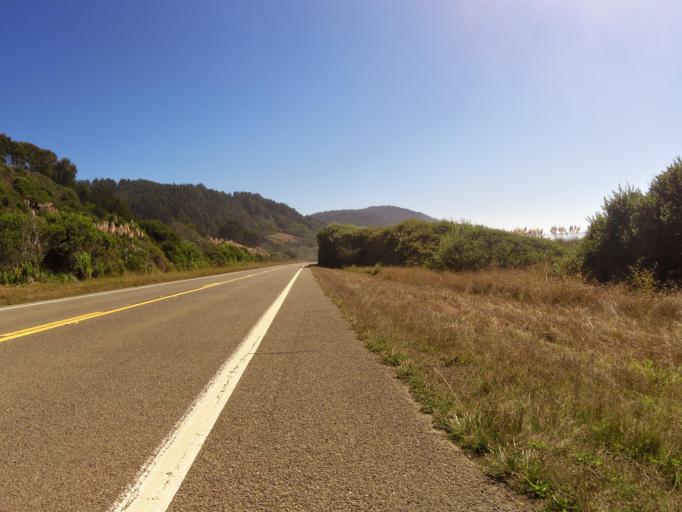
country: US
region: California
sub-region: Mendocino County
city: Fort Bragg
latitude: 39.6626
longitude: -123.7866
